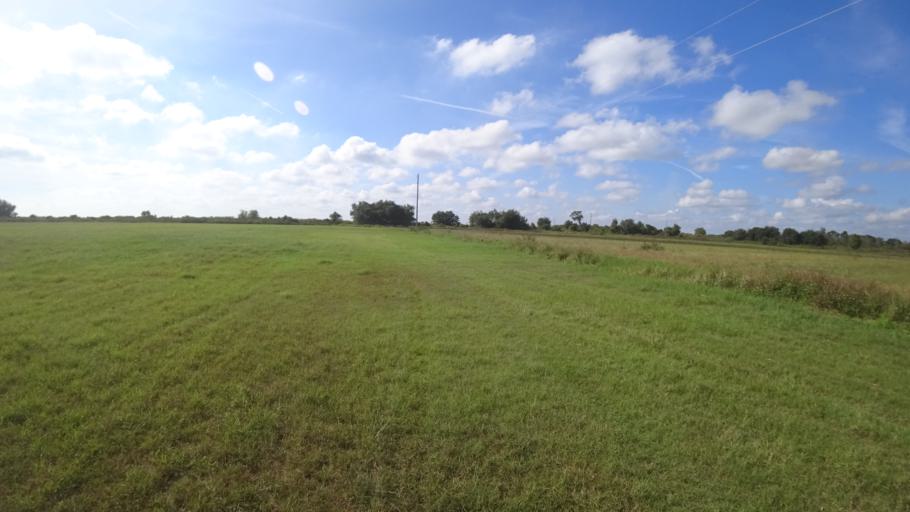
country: US
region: Florida
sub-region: Sarasota County
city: Lake Sarasota
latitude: 27.3733
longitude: -82.1688
